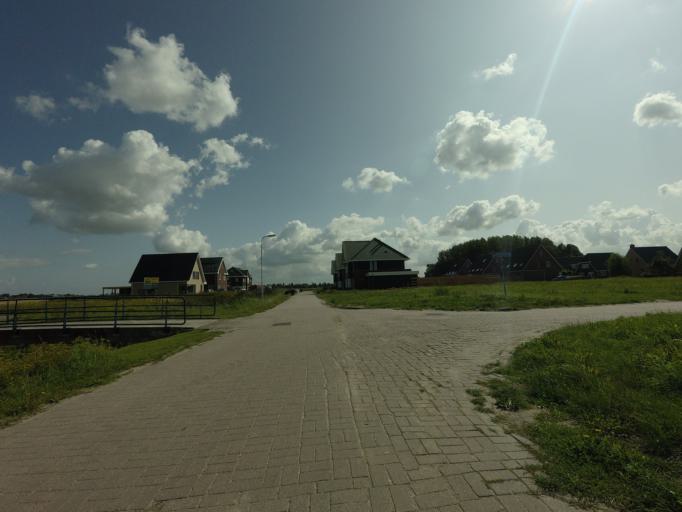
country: NL
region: Friesland
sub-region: Gemeente Het Bildt
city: Sint Annaparochie
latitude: 53.2824
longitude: 5.6587
